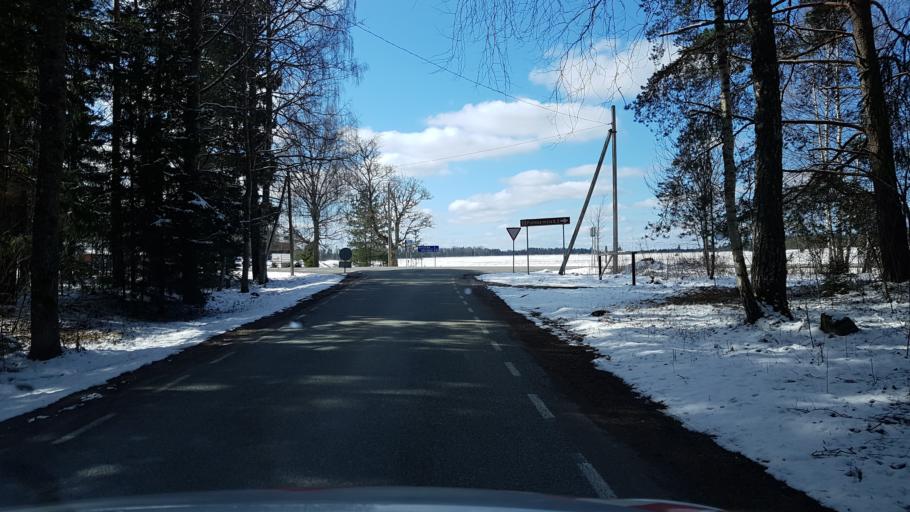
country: EE
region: Laeaene-Virumaa
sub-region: Tapa vald
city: Tapa
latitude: 59.5081
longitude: 25.9633
